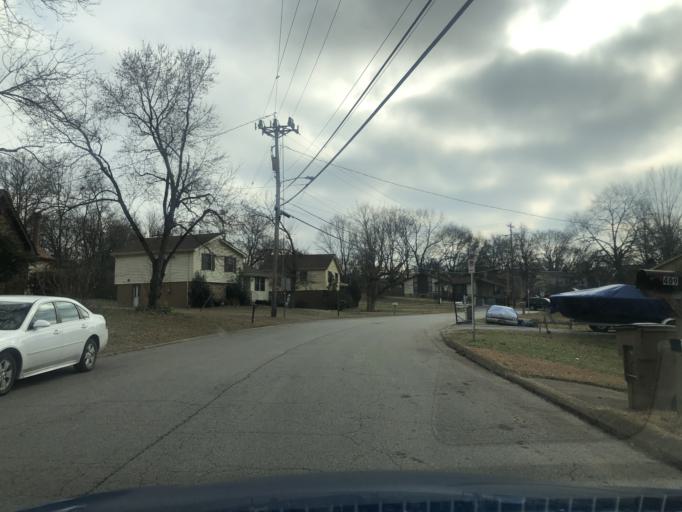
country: US
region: Tennessee
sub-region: Davidson County
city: Oak Hill
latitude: 36.0884
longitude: -86.7129
